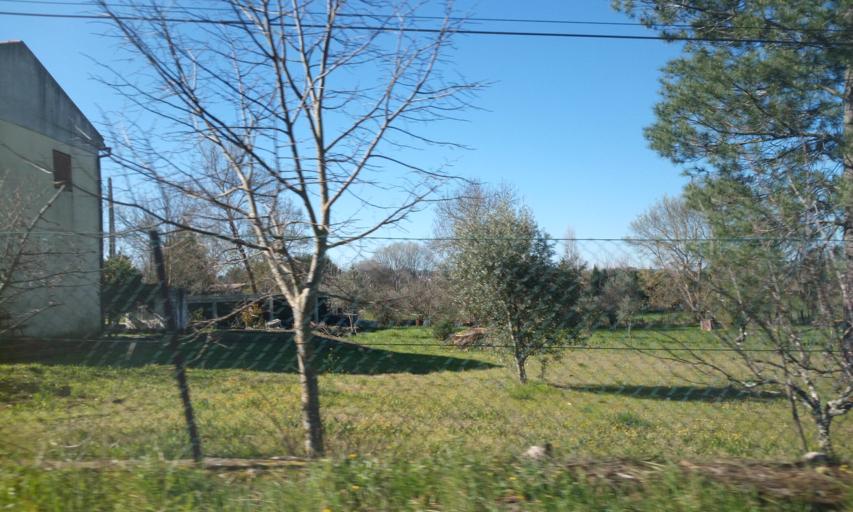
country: PT
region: Guarda
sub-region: Fornos de Algodres
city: Fornos de Algodres
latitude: 40.5310
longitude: -7.5599
